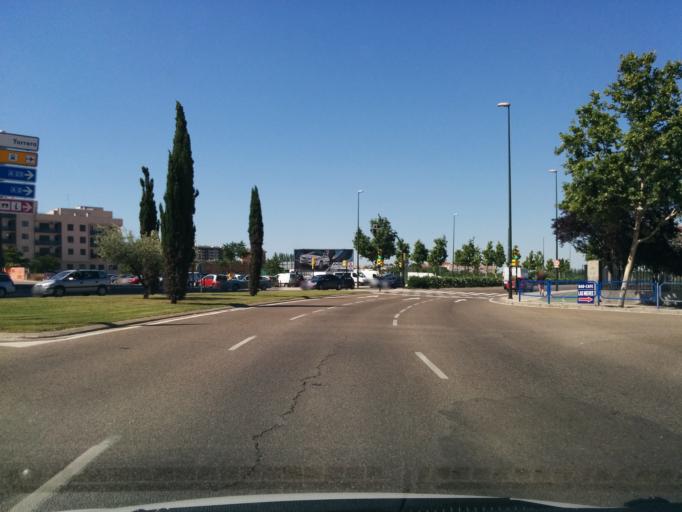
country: ES
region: Aragon
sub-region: Provincia de Zaragoza
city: Zaragoza
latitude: 41.6348
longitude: -0.8625
